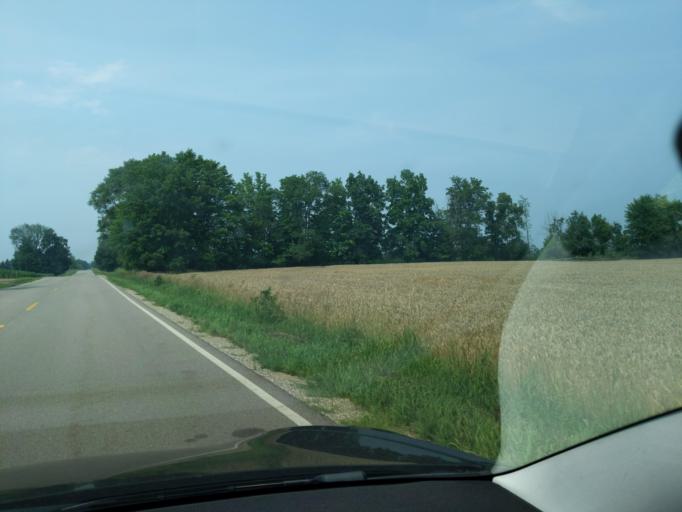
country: US
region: Michigan
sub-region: Clinton County
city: DeWitt
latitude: 42.9213
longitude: -84.5823
